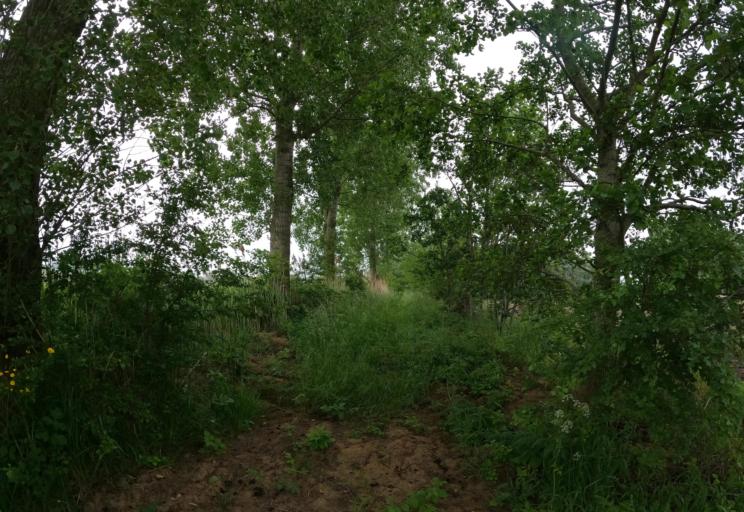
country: BE
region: Flanders
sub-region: Provincie Oost-Vlaanderen
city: Dendermonde
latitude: 51.0578
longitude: 4.0799
